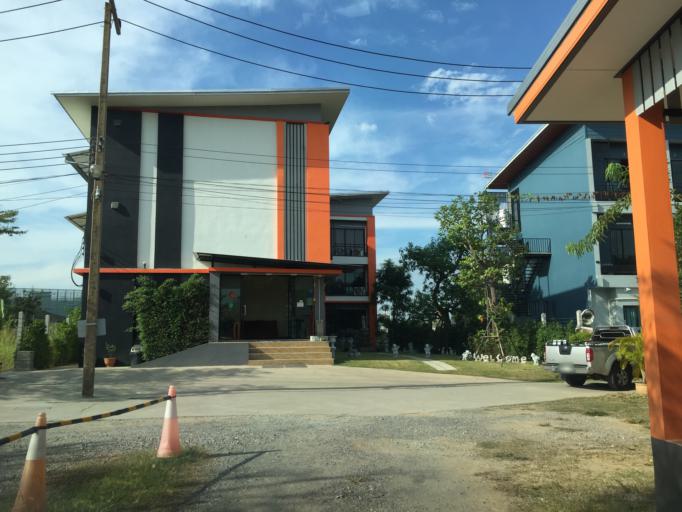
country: TH
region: Phitsanulok
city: Phitsanulok
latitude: 16.8433
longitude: 100.2340
